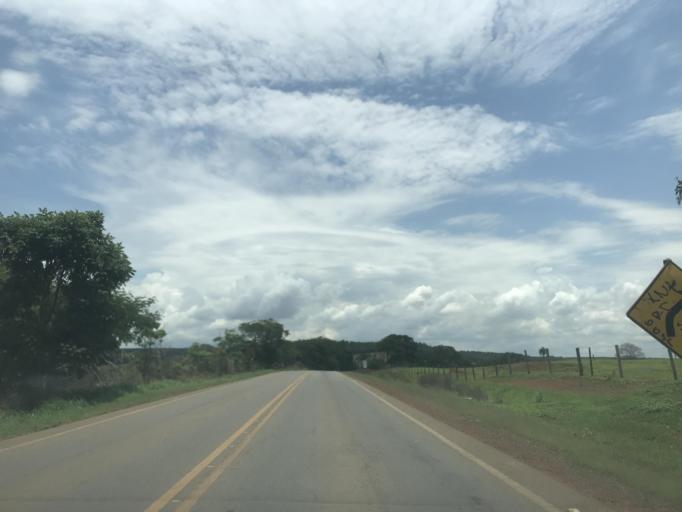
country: BR
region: Goias
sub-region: Vianopolis
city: Vianopolis
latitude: -16.7080
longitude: -48.3963
